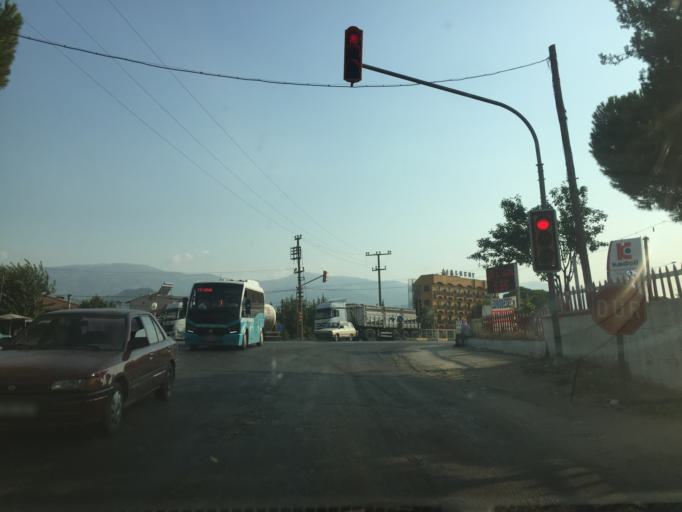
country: TR
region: Manisa
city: Salihli
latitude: 38.4954
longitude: 28.1814
